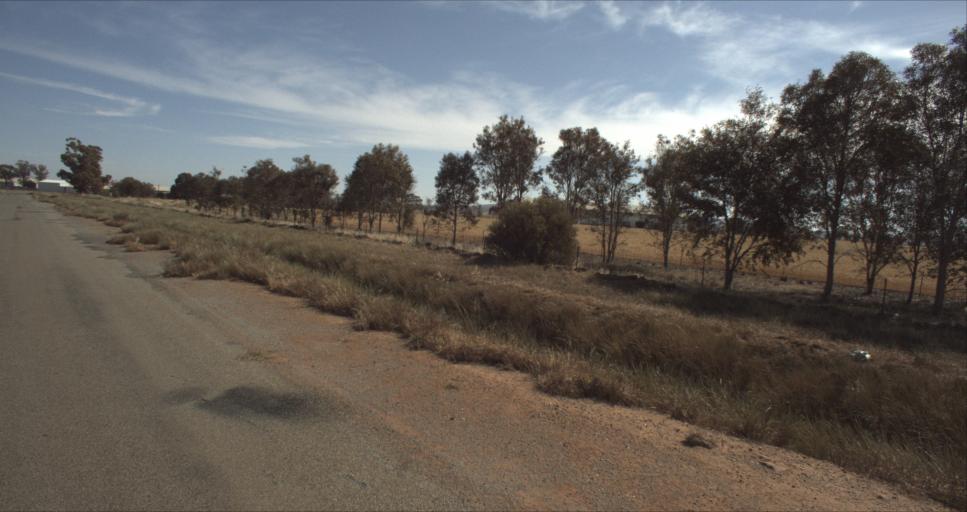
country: AU
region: New South Wales
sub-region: Leeton
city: Leeton
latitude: -34.5619
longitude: 146.4693
